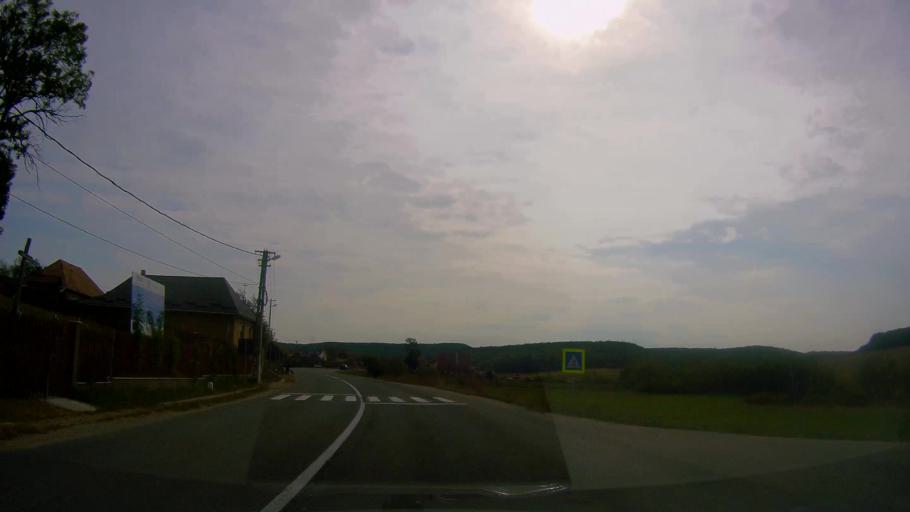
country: RO
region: Salaj
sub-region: Comuna Romanasi
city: Romanasi
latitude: 47.0817
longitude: 23.1908
